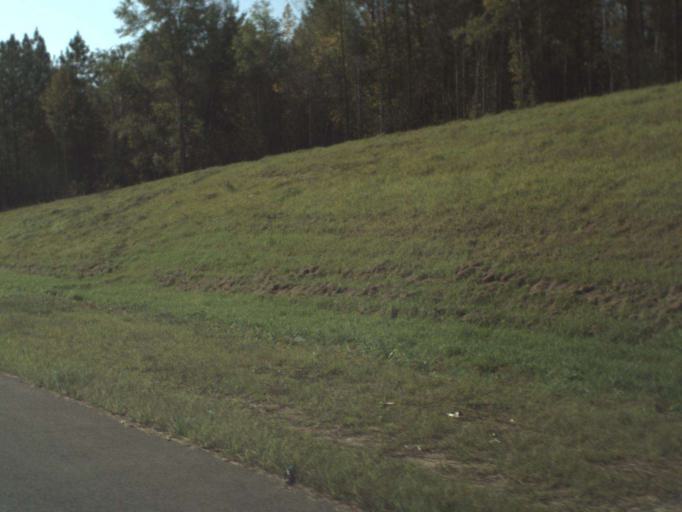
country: US
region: Florida
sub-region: Gadsden County
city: Quincy
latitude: 30.5802
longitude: -84.5490
